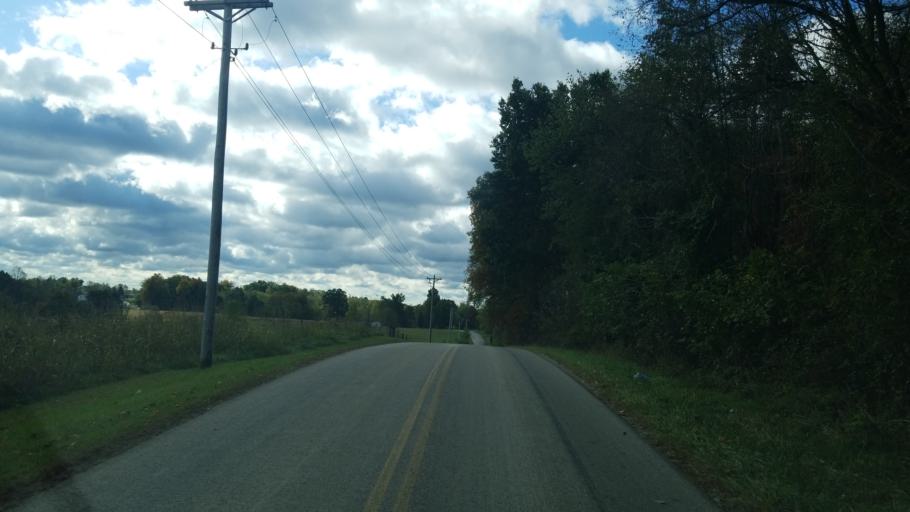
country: US
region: Ohio
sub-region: Vinton County
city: McArthur
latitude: 39.2308
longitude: -82.5086
